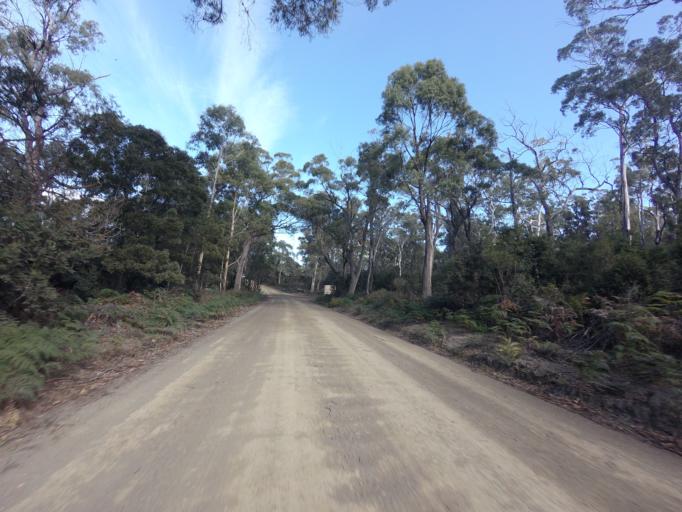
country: AU
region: Tasmania
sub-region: Clarence
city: Sandford
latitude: -42.9909
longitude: 147.7137
